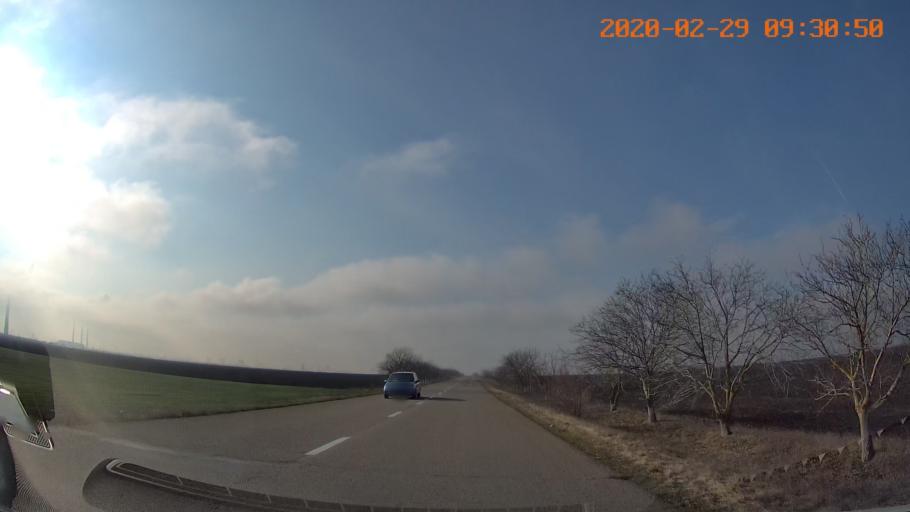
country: MD
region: Telenesti
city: Dnestrovsc
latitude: 46.6611
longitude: 29.9145
